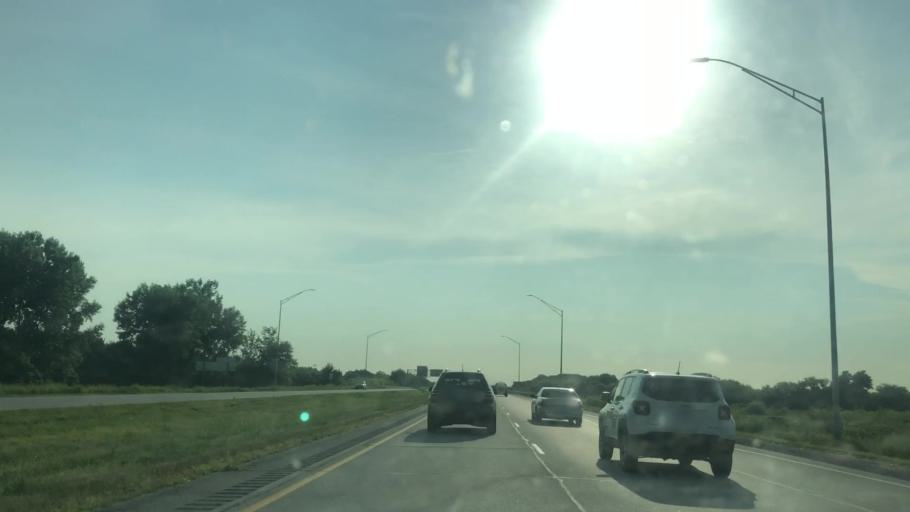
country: US
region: Iowa
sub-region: Story County
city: Ames
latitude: 42.0064
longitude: -93.5912
